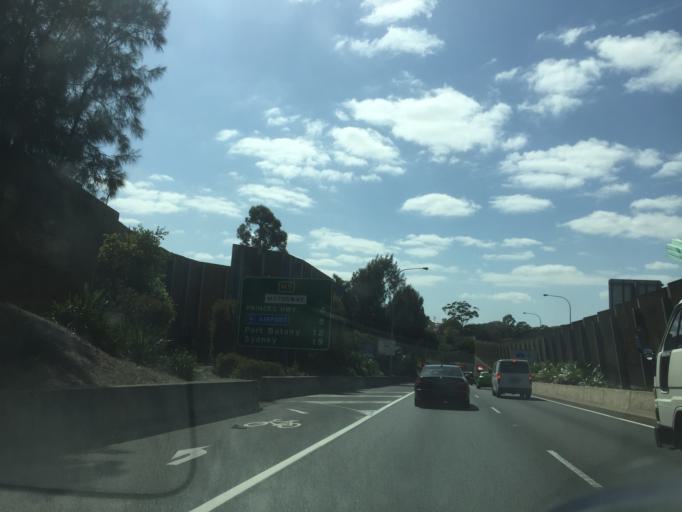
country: AU
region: New South Wales
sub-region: Rockdale
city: Bexley North
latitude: -33.9362
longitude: 151.1086
